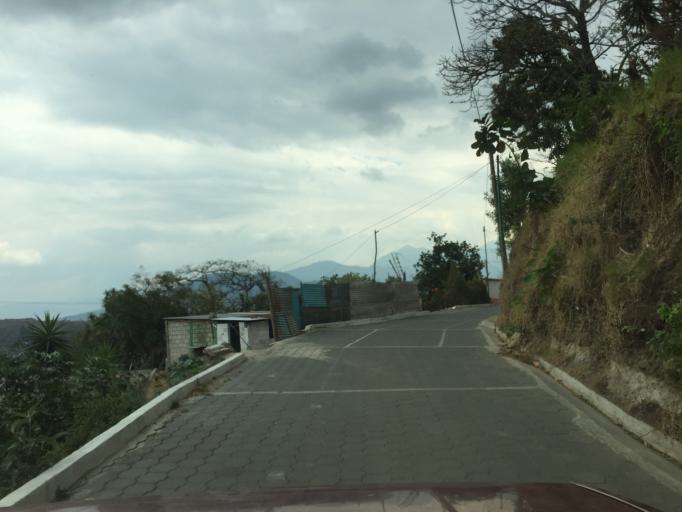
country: GT
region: Guatemala
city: Amatitlan
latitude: 14.4931
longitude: -90.6418
